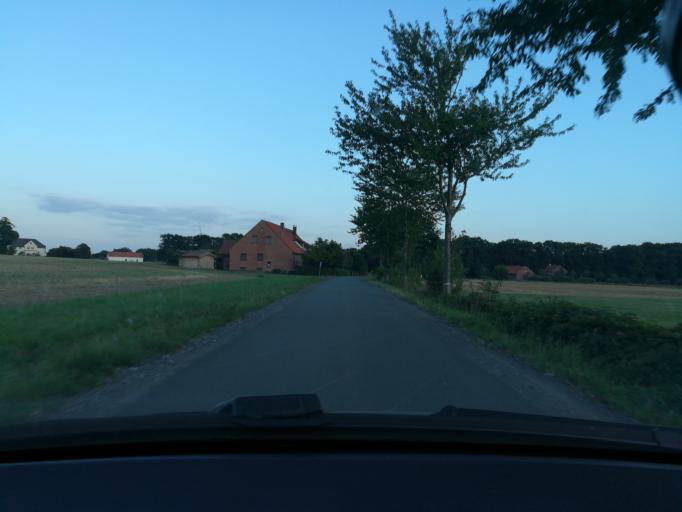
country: DE
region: North Rhine-Westphalia
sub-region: Regierungsbezirk Munster
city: Lienen
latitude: 52.1395
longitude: 7.9907
